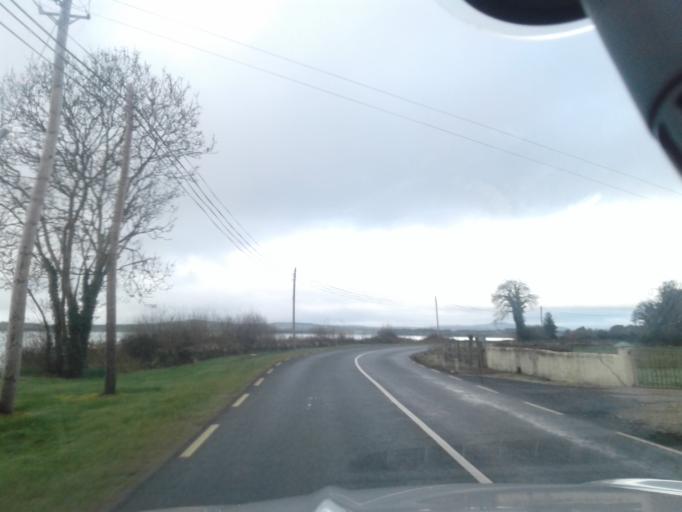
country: IE
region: Ulster
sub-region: County Donegal
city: Ramelton
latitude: 55.0839
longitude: -7.5771
